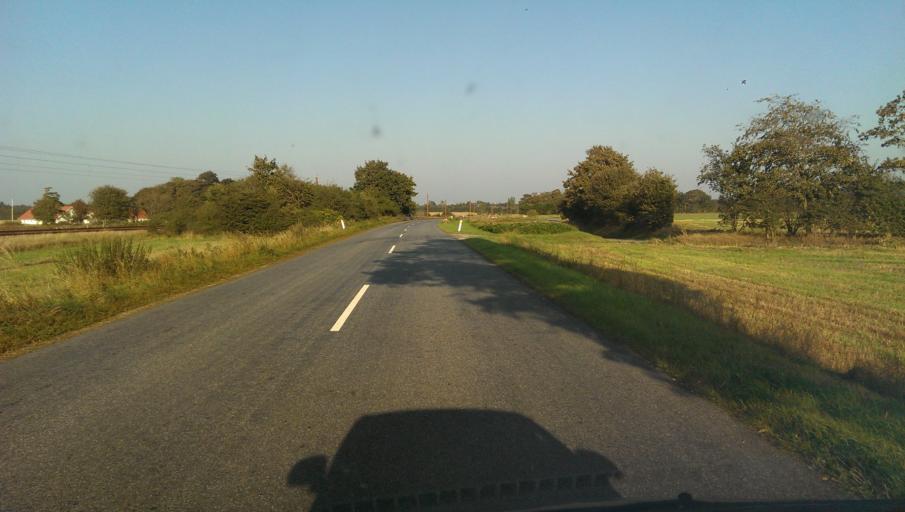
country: DK
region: South Denmark
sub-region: Esbjerg Kommune
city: Bramming
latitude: 55.4667
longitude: 8.7477
